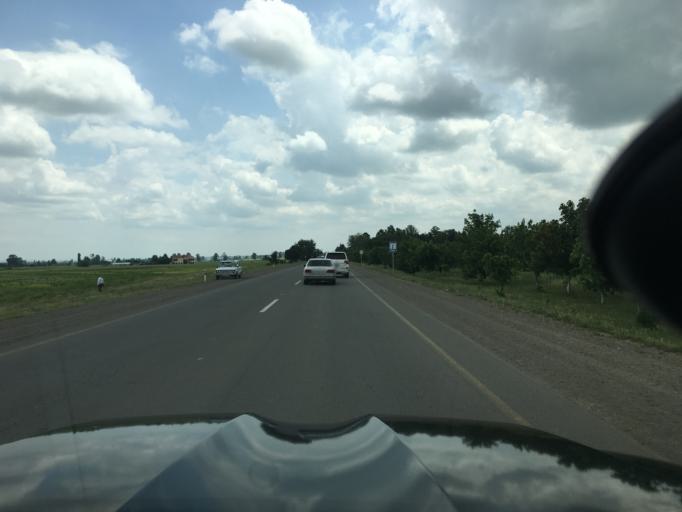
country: AZ
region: Tovuz
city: Tovuz
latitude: 40.9614
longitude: 45.7183
